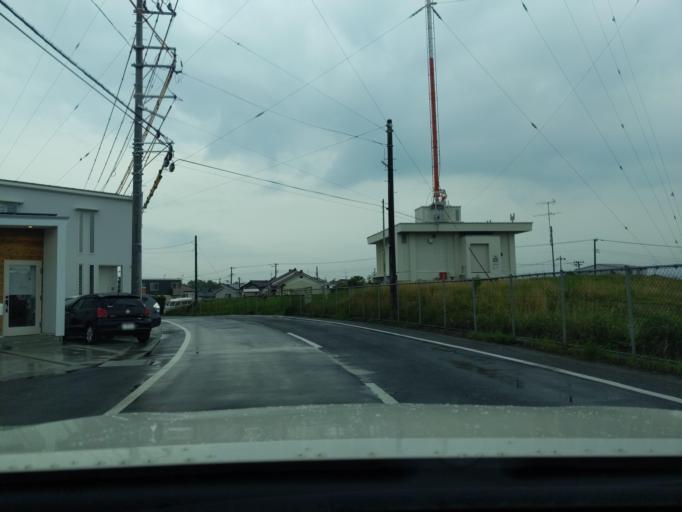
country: JP
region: Fukushima
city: Koriyama
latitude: 37.3604
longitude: 140.3550
